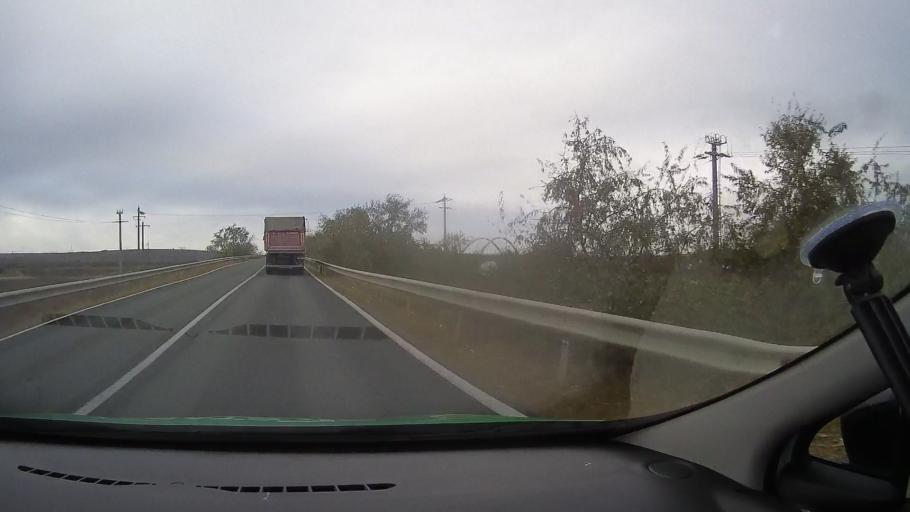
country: RO
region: Constanta
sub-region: Comuna Poarta Alba
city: Poarta Alba
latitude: 44.2143
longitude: 28.3925
